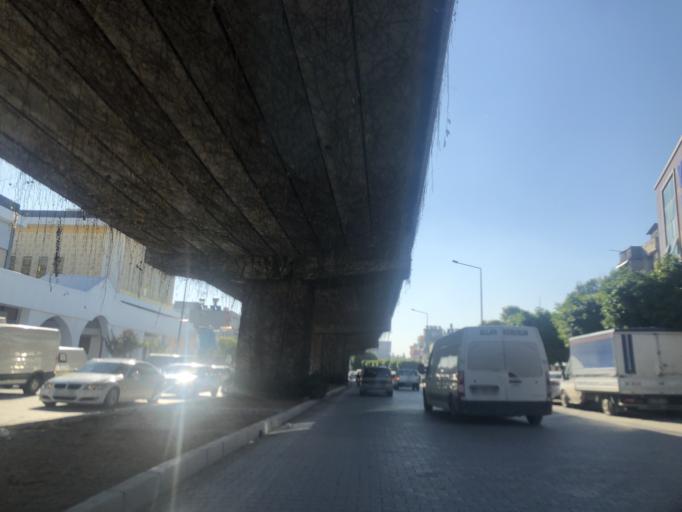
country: TR
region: Adana
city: Seyhan
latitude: 36.9872
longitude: 35.3186
